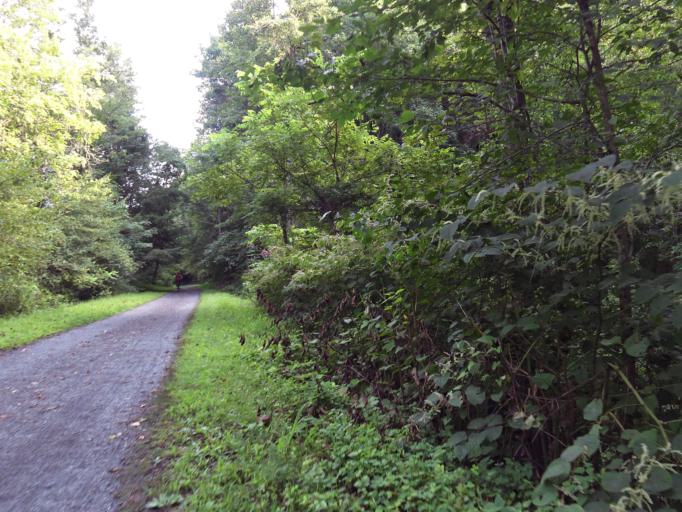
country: US
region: Virginia
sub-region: Washington County
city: Abingdon
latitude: 36.6930
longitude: -81.9405
